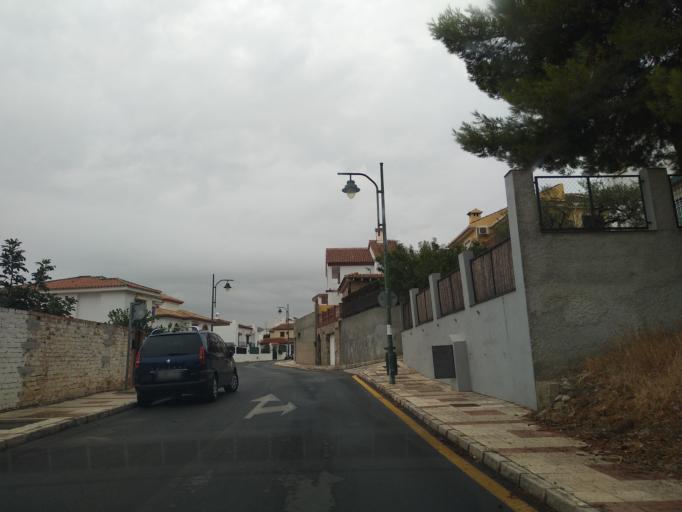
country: ES
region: Andalusia
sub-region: Provincia de Malaga
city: Malaga
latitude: 36.7411
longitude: -4.4764
